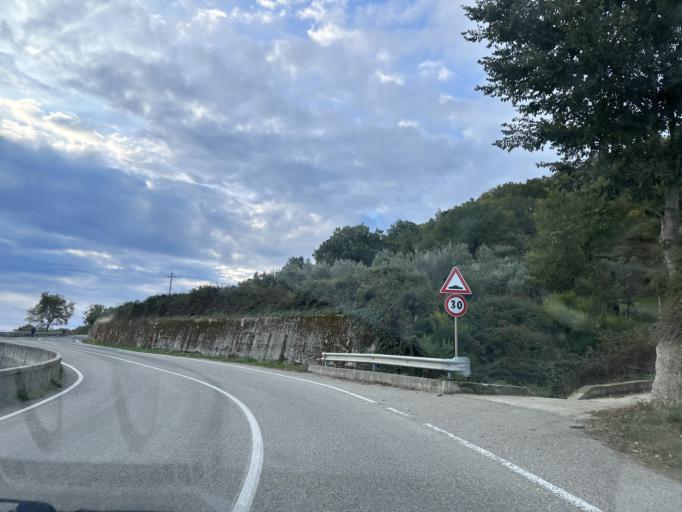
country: IT
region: Calabria
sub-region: Provincia di Catanzaro
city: Montauro
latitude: 38.7546
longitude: 16.5062
